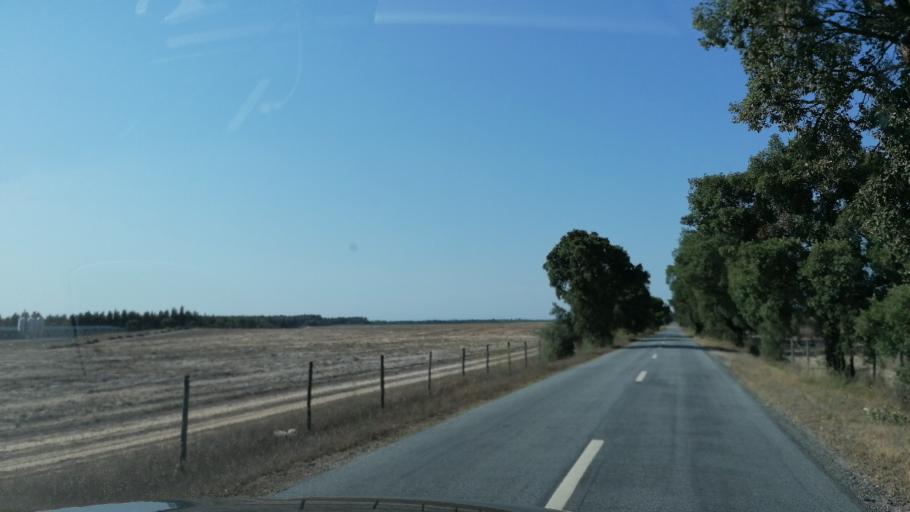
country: PT
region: Evora
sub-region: Vendas Novas
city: Vendas Novas
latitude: 38.7233
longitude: -8.6203
